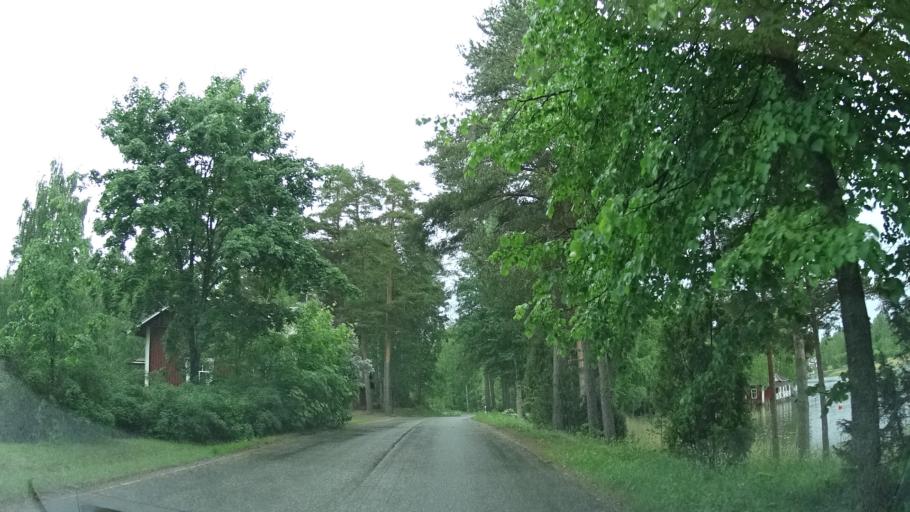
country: FI
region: Paijanne Tavastia
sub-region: Lahti
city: Sysmae
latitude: 61.4938
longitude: 25.5809
